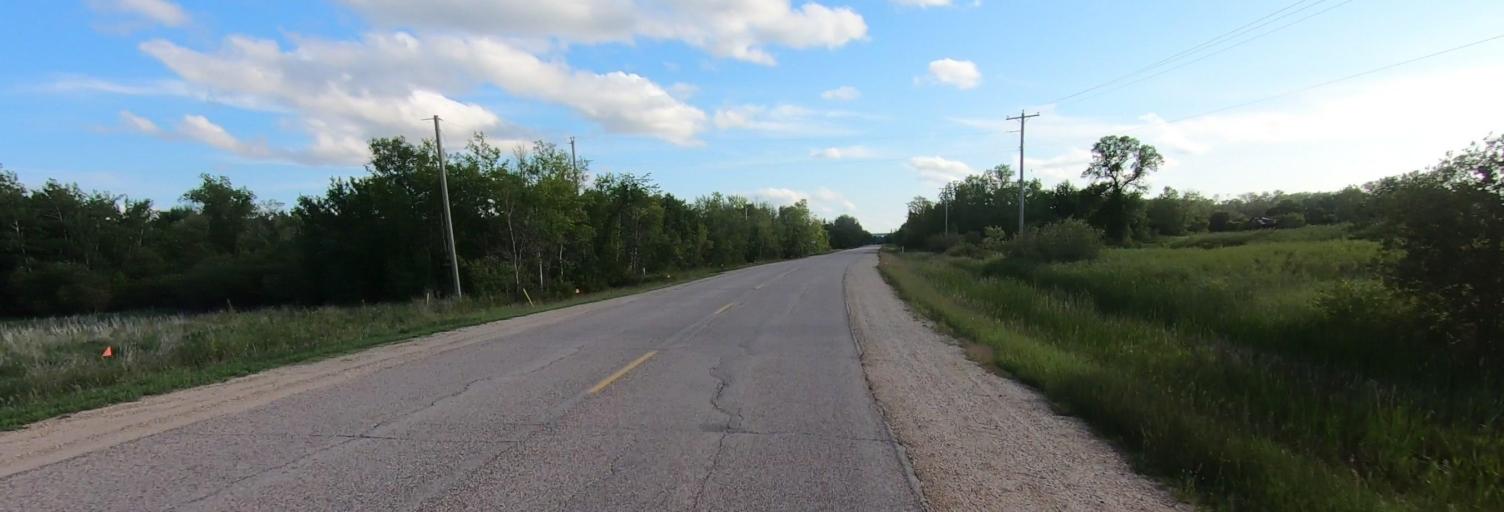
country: CA
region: Manitoba
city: Selkirk
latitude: 50.2008
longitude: -96.8392
